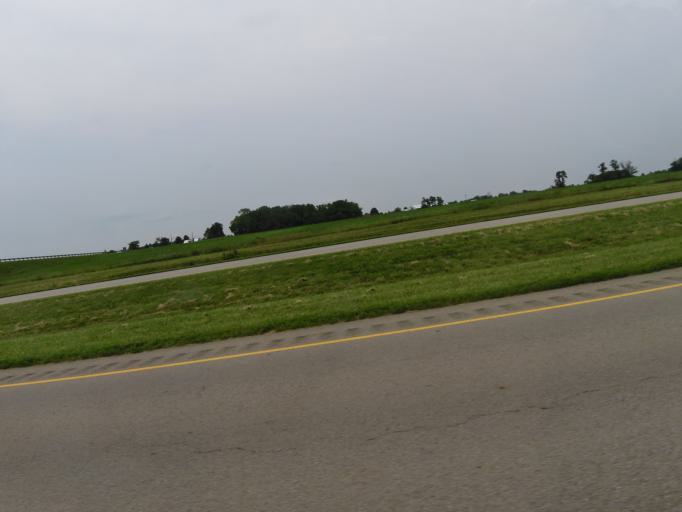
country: US
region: Ohio
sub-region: Clinton County
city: Wilmington
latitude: 39.4643
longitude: -83.8523
